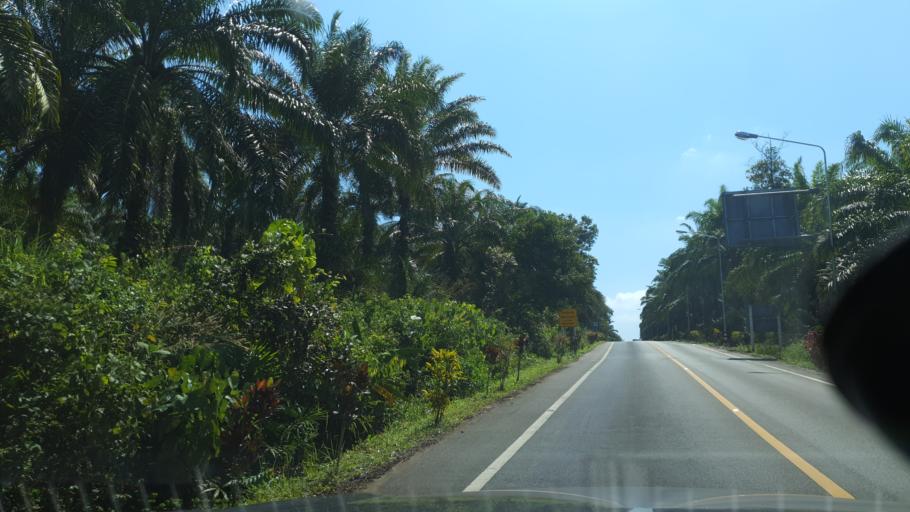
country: TH
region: Krabi
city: Khlong Thom
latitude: 7.9453
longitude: 99.2154
